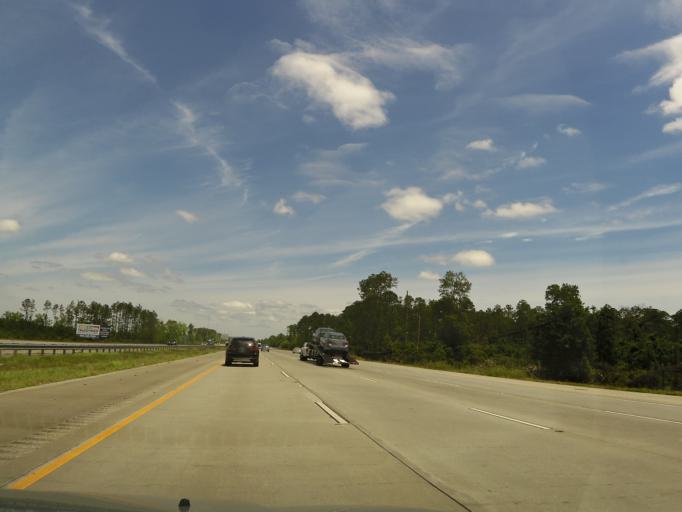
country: US
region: Georgia
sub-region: Glynn County
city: Country Club Estates
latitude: 31.2639
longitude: -81.4939
